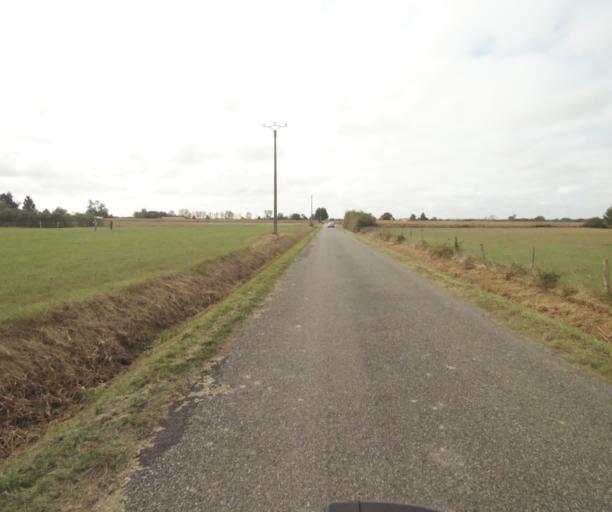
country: FR
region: Midi-Pyrenees
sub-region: Departement du Tarn-et-Garonne
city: Finhan
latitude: 43.9201
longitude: 1.2432
